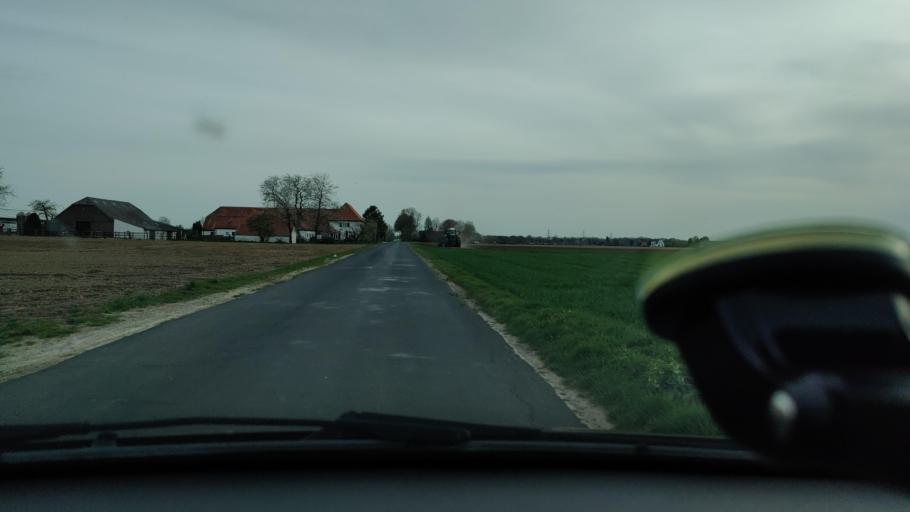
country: DE
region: North Rhine-Westphalia
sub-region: Regierungsbezirk Dusseldorf
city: Goch
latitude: 51.7087
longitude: 6.1813
